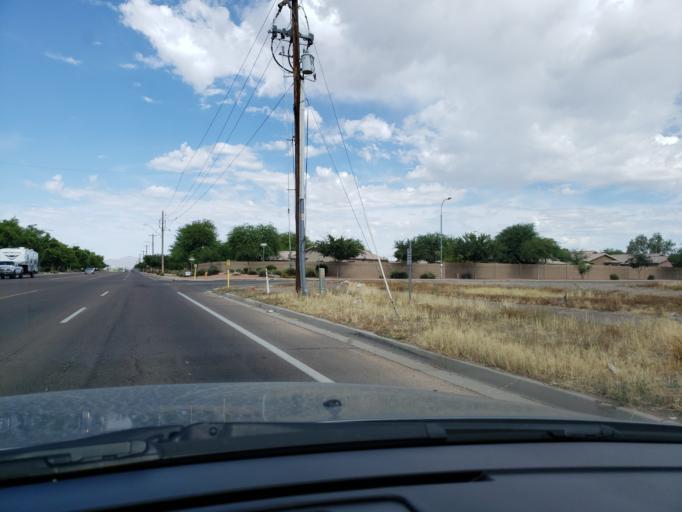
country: US
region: Arizona
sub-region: Maricopa County
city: Peoria
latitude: 33.5520
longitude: -112.2459
